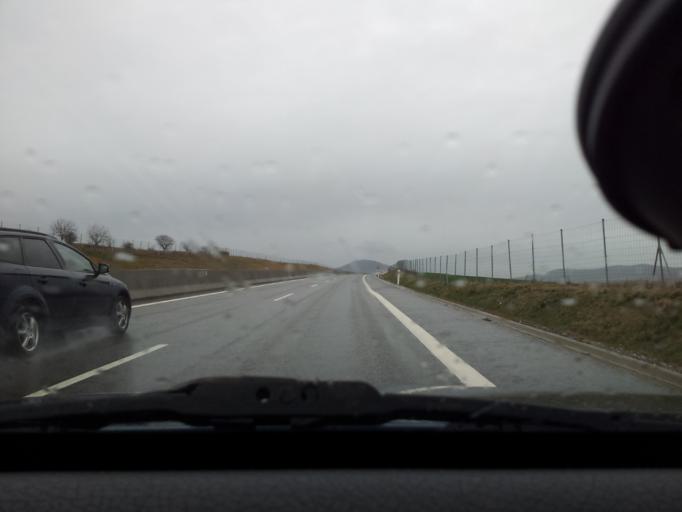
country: SK
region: Nitriansky
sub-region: Okres Nitra
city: Vrable
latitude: 48.3357
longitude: 18.2545
